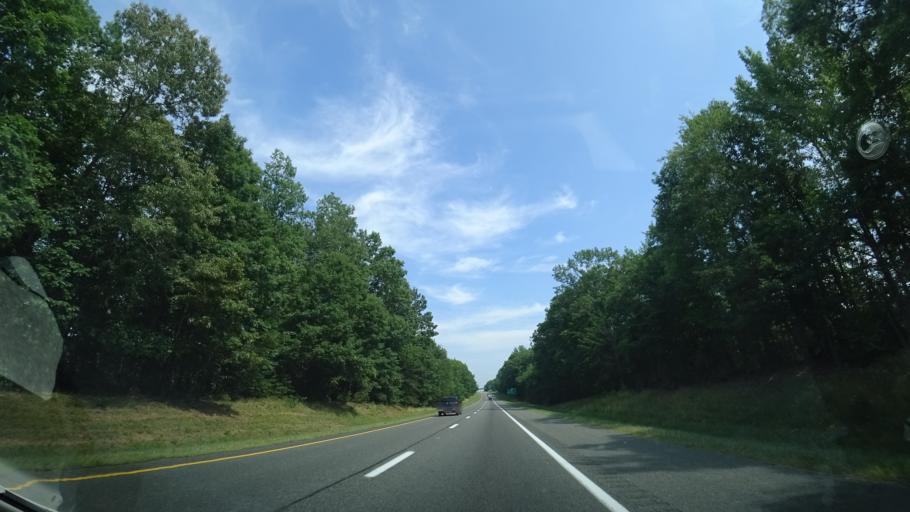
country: US
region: Virginia
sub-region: Louisa County
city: Louisa
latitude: 37.8907
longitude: -78.0389
